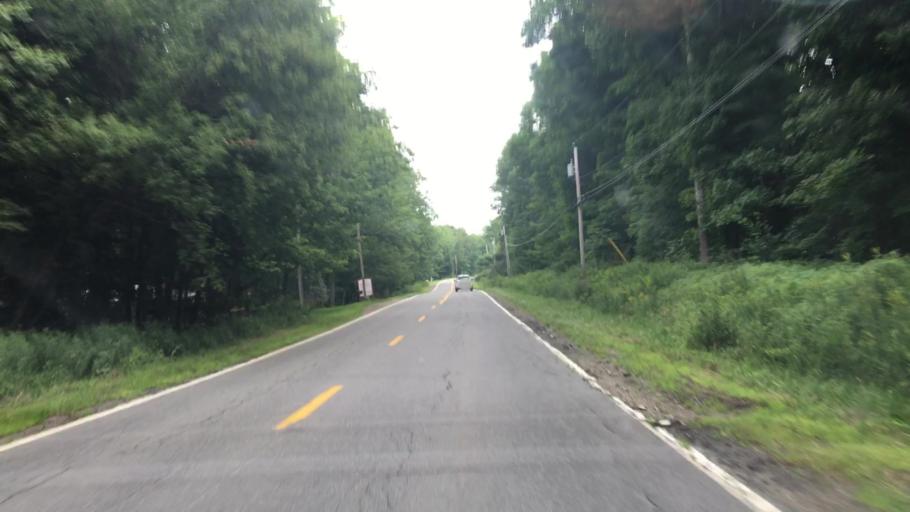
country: US
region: Maine
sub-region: Kennebec County
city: Vassalboro
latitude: 44.4348
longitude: -69.5971
